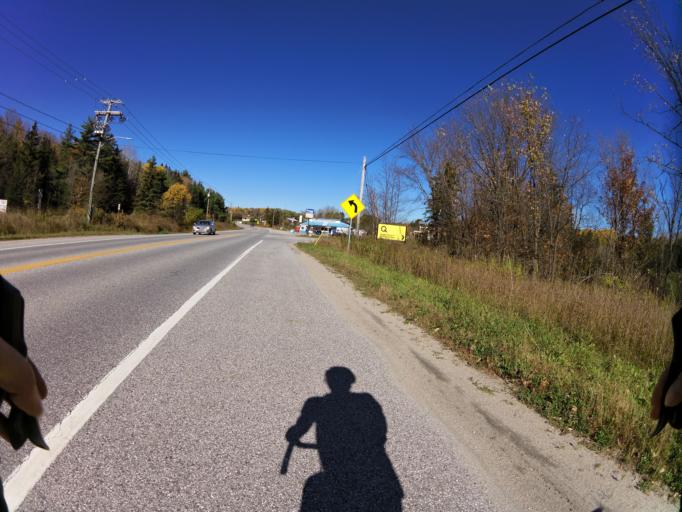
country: CA
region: Quebec
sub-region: Outaouais
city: Wakefield
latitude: 45.8046
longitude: -75.9462
